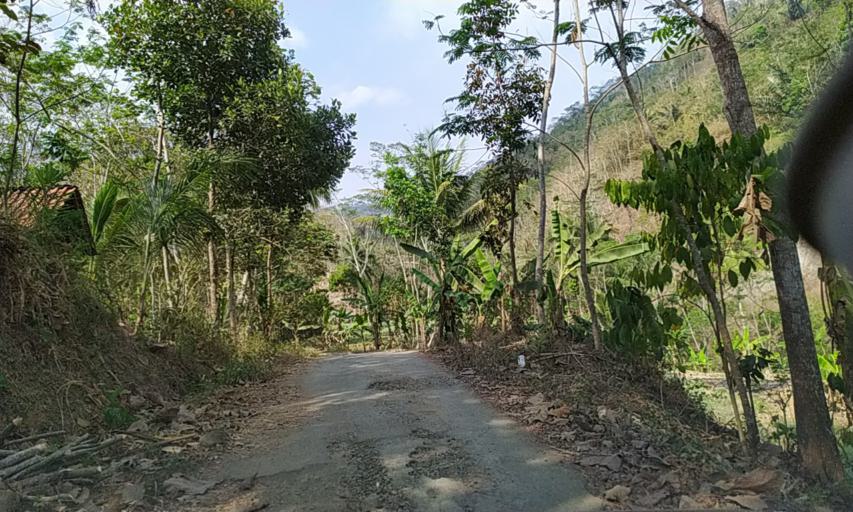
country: ID
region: Central Java
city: Bantarmangu
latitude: -7.3325
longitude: 108.9000
